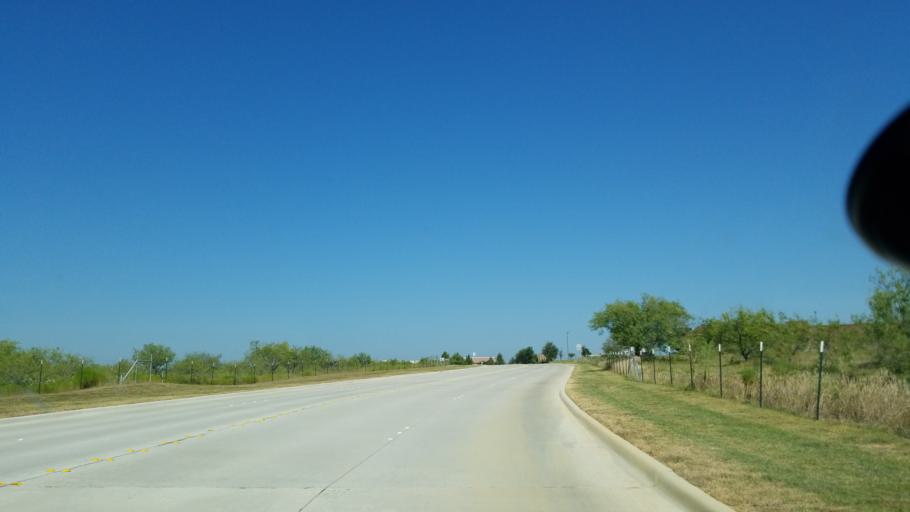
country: US
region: Texas
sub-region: Tarrant County
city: Mansfield
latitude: 32.5609
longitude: -97.1029
